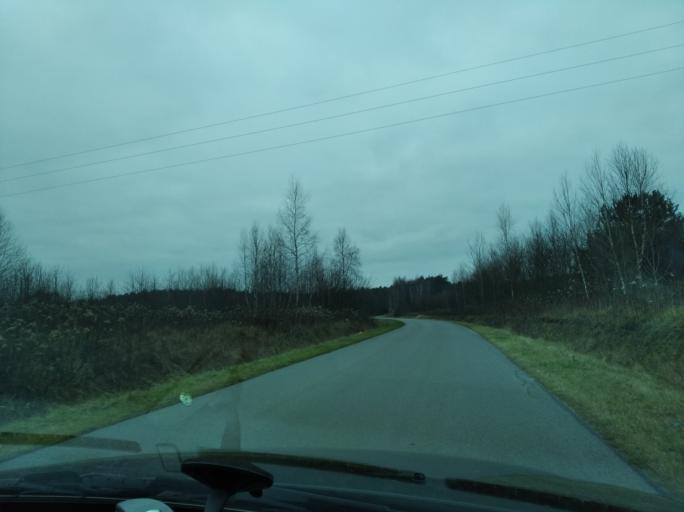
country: PL
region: Subcarpathian Voivodeship
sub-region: Powiat lancucki
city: Brzoza Stadnicka
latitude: 50.2008
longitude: 22.2809
